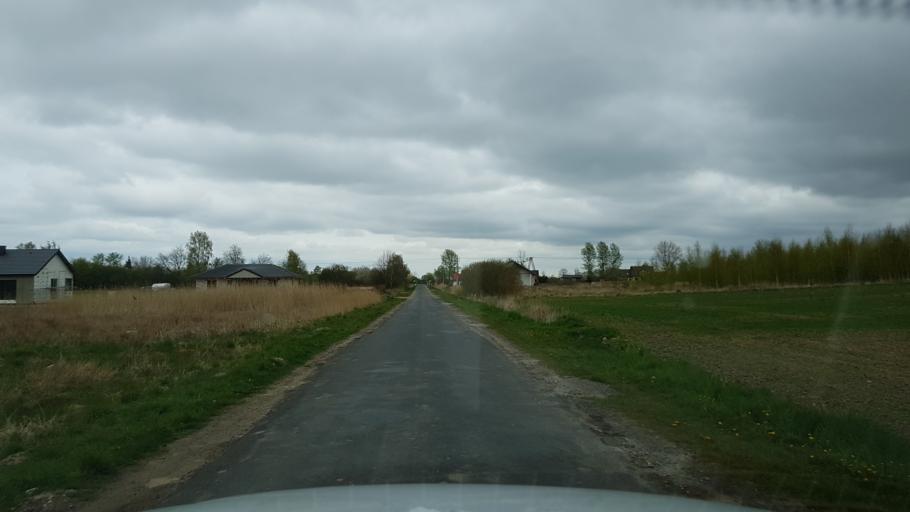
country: PL
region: West Pomeranian Voivodeship
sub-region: Powiat koszalinski
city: Mielno
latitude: 54.2360
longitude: 16.0635
